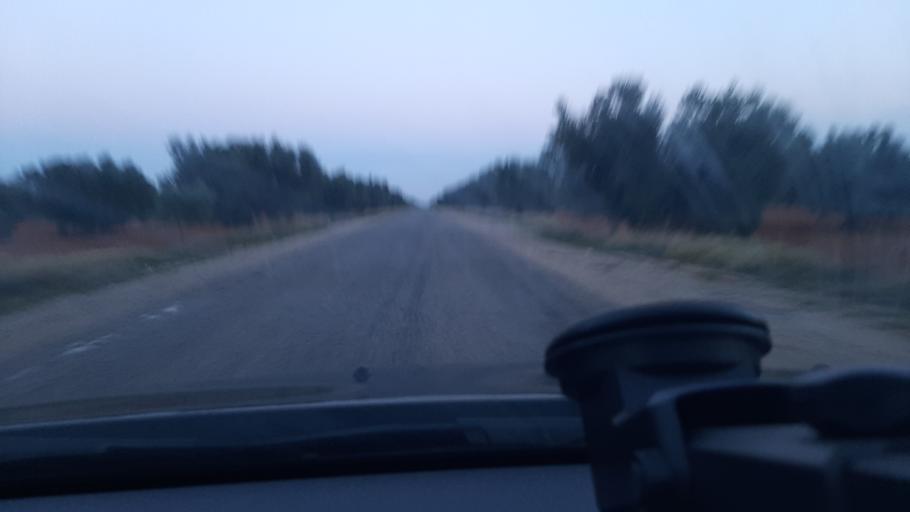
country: TN
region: Al Mahdiyah
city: Shurban
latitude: 35.0311
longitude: 10.4943
